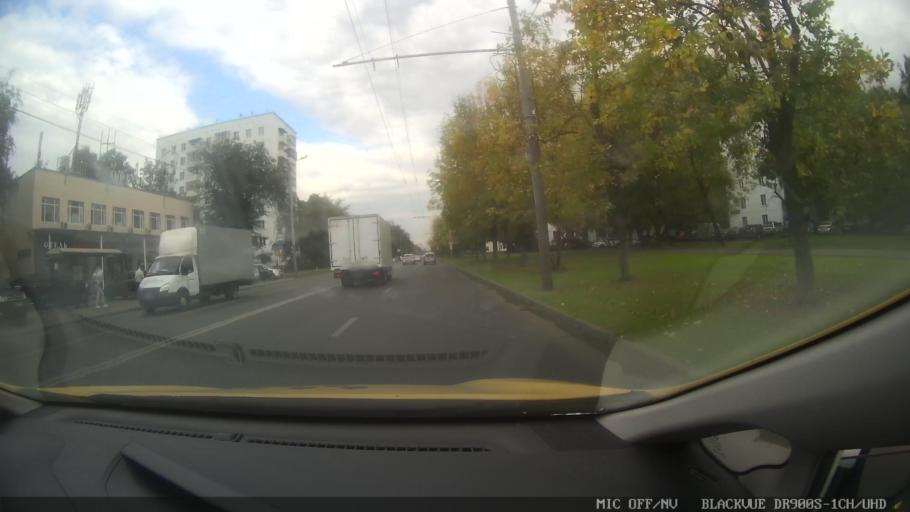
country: RU
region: Moscow
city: Novyye Kuz'minki
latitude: 55.6999
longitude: 37.7684
